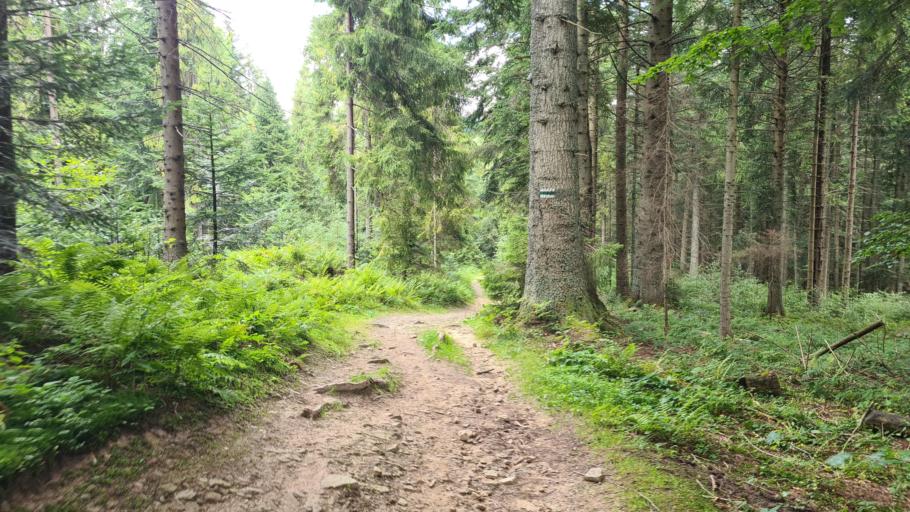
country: PL
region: Lesser Poland Voivodeship
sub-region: Powiat nowosadecki
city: Rytro
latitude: 49.4133
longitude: 20.6226
